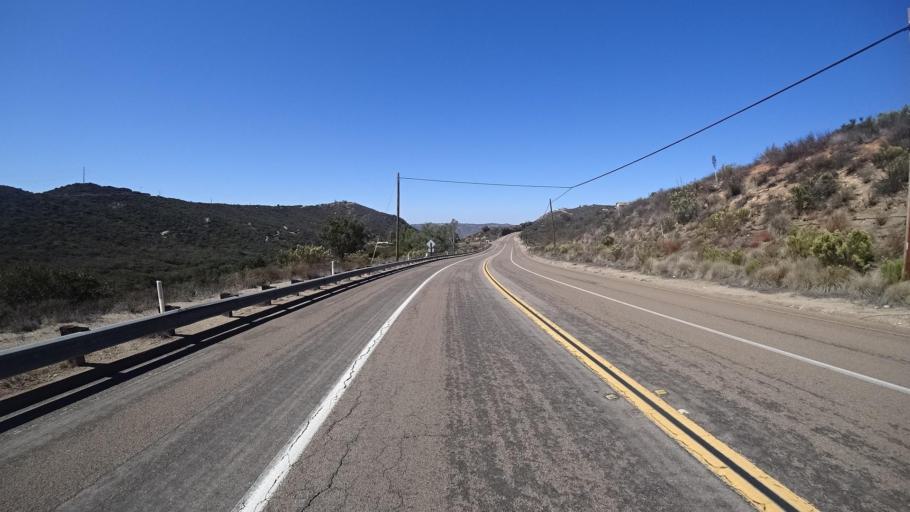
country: US
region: California
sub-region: San Diego County
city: Alpine
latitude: 32.8029
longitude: -116.7736
